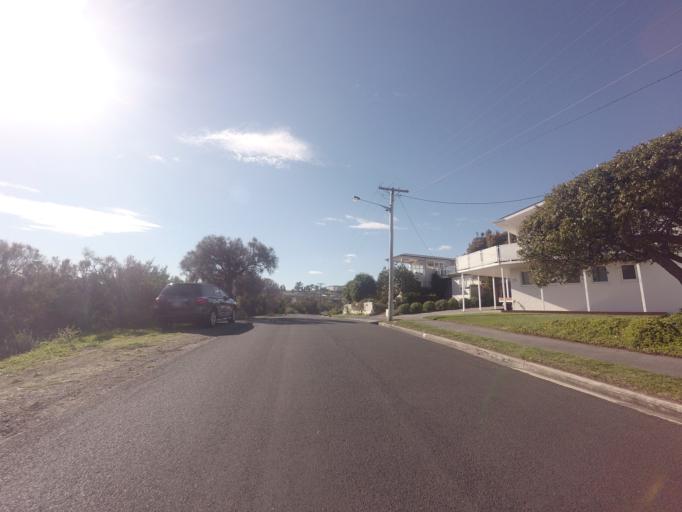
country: AU
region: Tasmania
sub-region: Clarence
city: Bellerive
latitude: -42.8675
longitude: 147.3538
